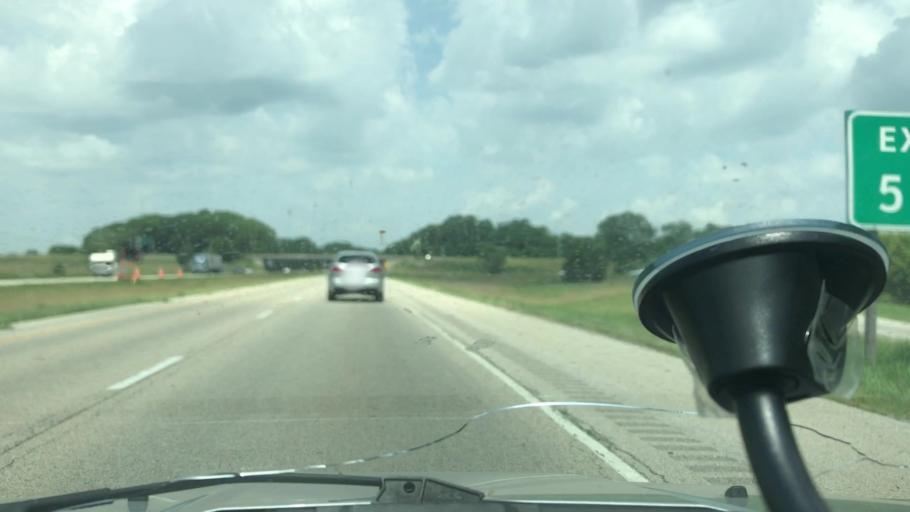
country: US
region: Illinois
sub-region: Peoria County
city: Bellevue
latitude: 40.6707
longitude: -89.6655
